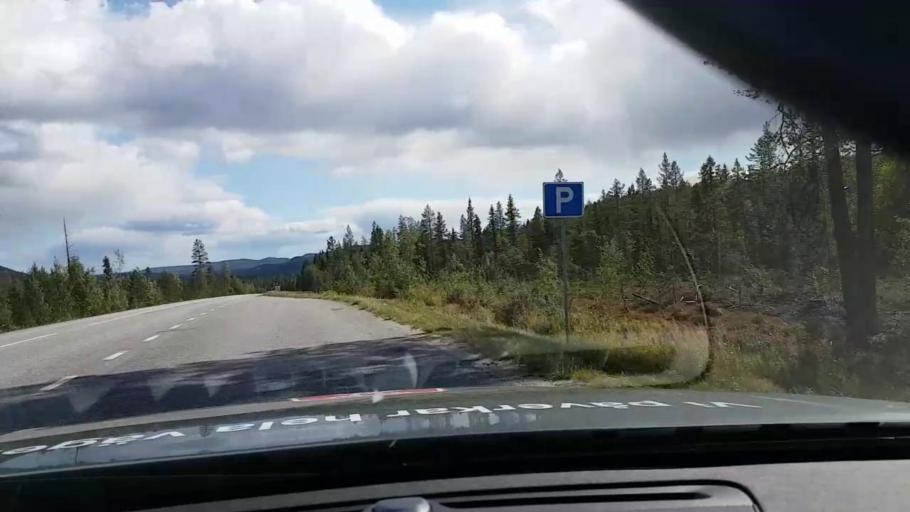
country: SE
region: Vaesterbotten
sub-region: Asele Kommun
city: Asele
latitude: 63.7688
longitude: 17.6823
